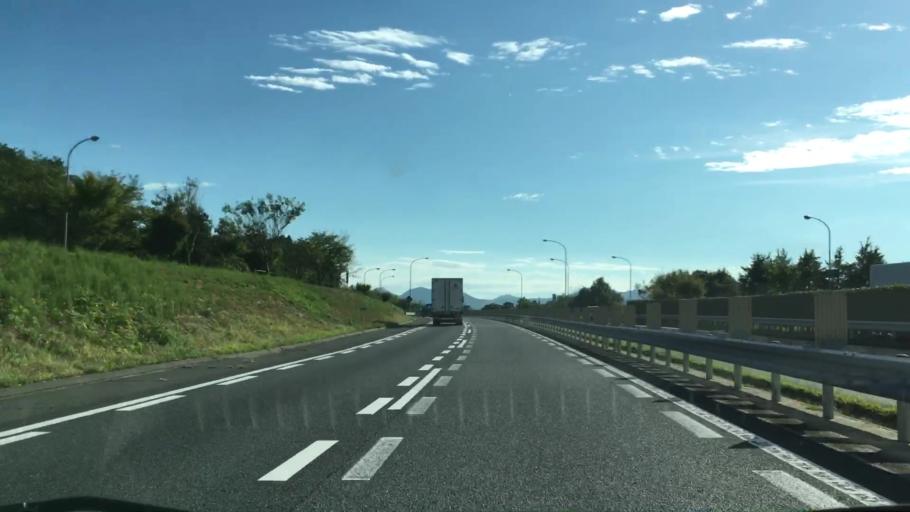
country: JP
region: Yamaguchi
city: Yanai
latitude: 34.0996
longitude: 132.1018
